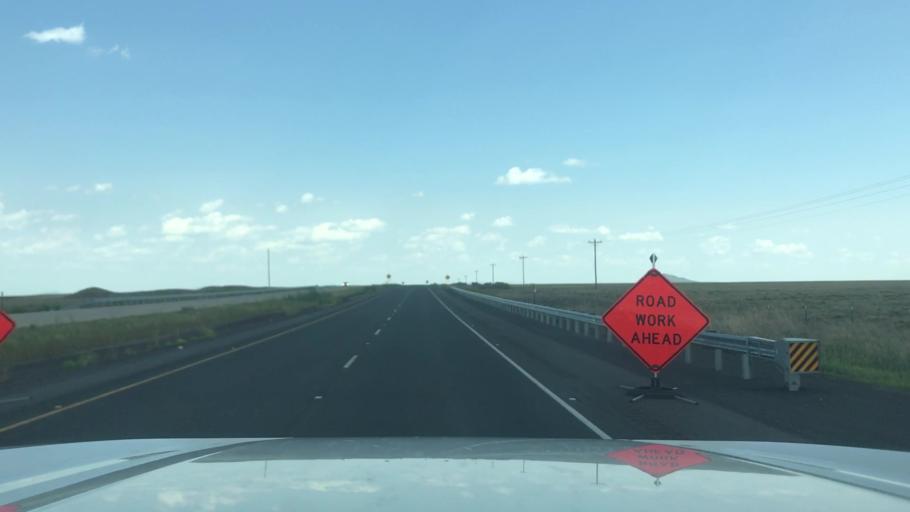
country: US
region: New Mexico
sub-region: Union County
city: Clayton
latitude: 36.6253
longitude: -103.7037
